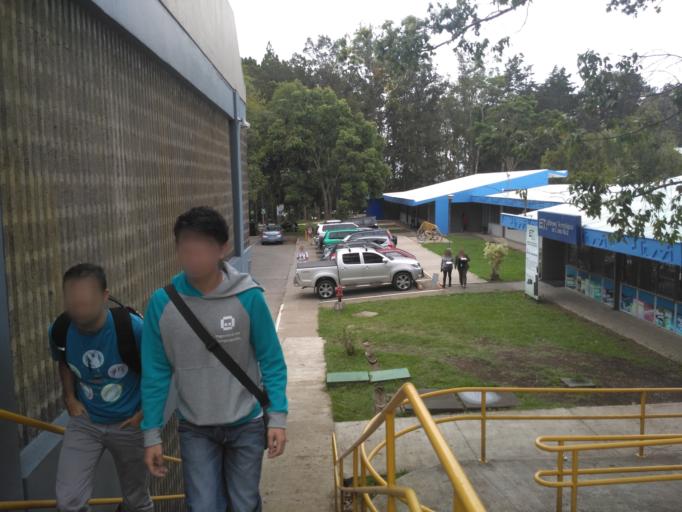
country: CR
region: Cartago
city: Cartago
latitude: 9.8567
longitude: -83.9124
